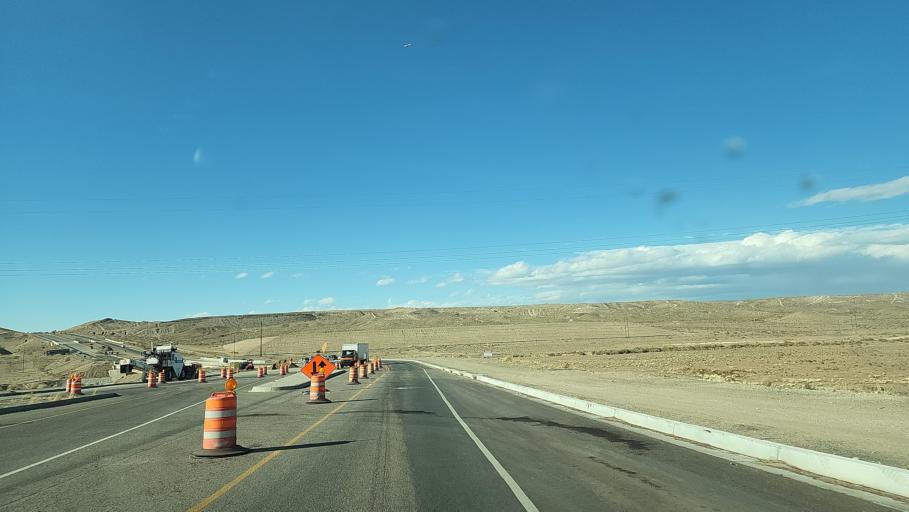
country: US
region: New Mexico
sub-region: Bernalillo County
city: South Valley
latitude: 35.0083
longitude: -106.6264
